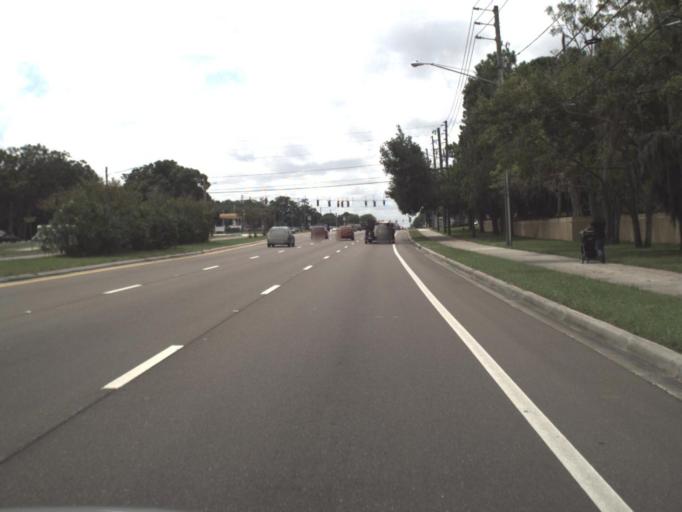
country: US
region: Florida
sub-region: Pinellas County
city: Safety Harbor
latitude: 28.0169
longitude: -82.7091
